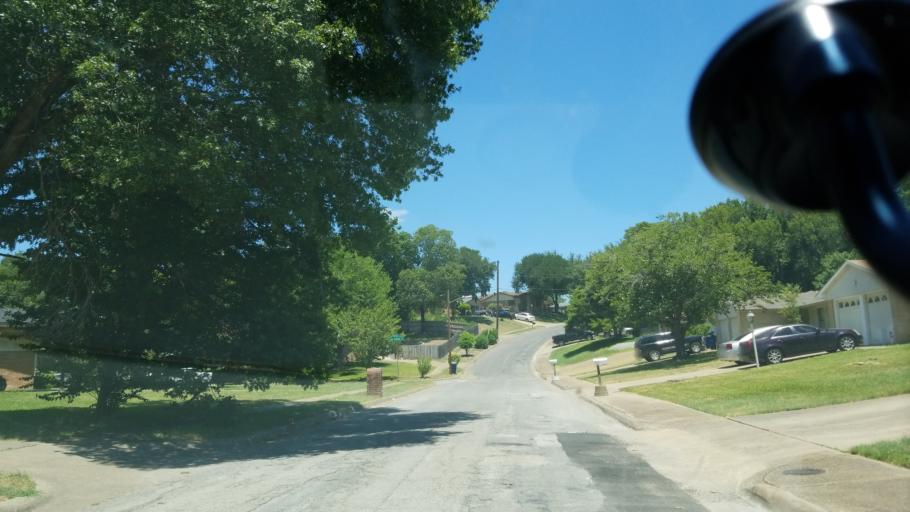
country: US
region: Texas
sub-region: Dallas County
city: Cockrell Hill
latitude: 32.6947
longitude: -96.8320
